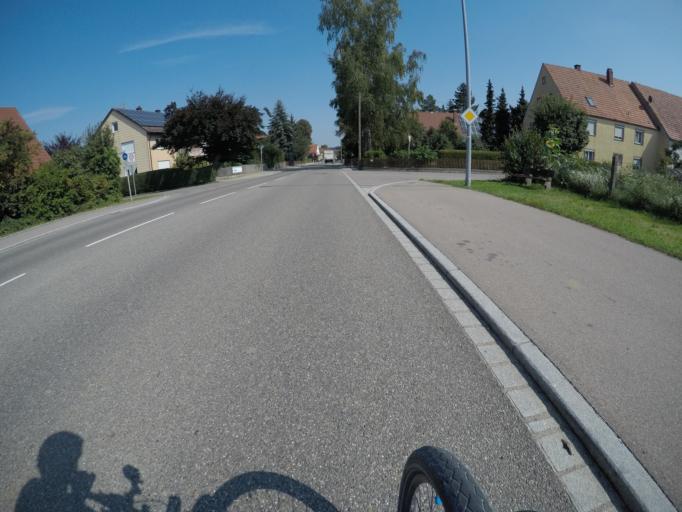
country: DE
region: Bavaria
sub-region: Swabia
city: Binswangen
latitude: 48.5553
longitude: 10.6356
